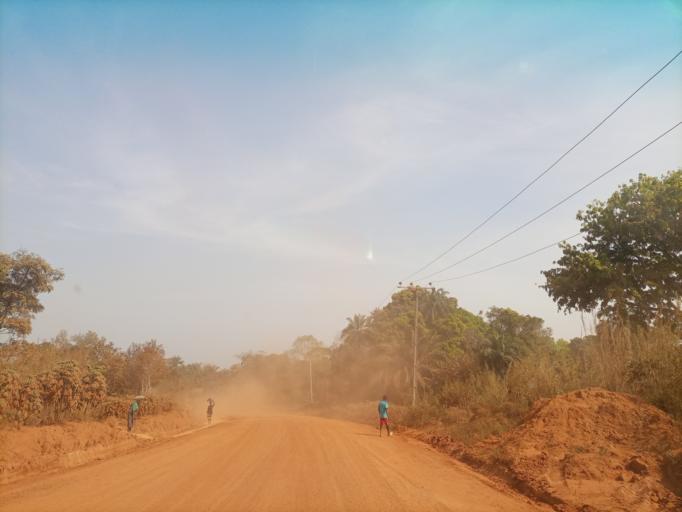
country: NG
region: Enugu
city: Eha Amufu
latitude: 6.6680
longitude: 7.7493
